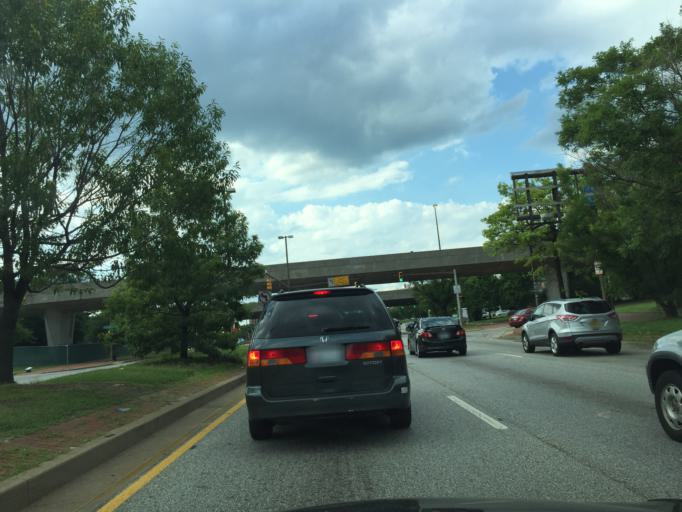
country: US
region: Maryland
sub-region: City of Baltimore
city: Baltimore
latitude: 39.2932
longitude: -76.6277
